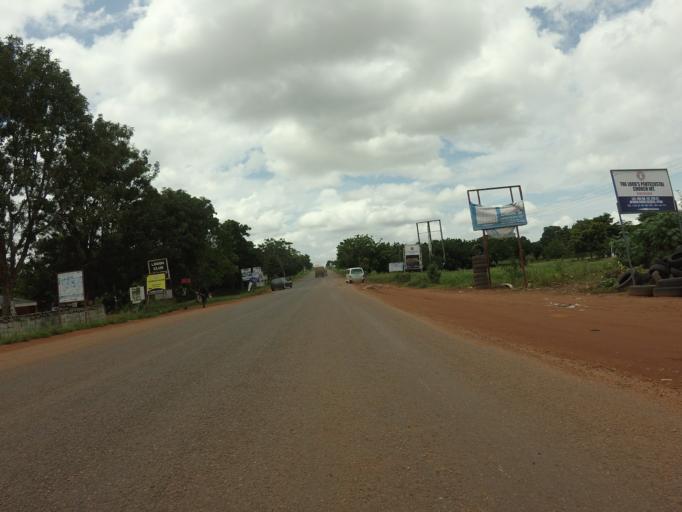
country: GH
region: Eastern
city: Aburi
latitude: 5.8038
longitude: -0.1256
